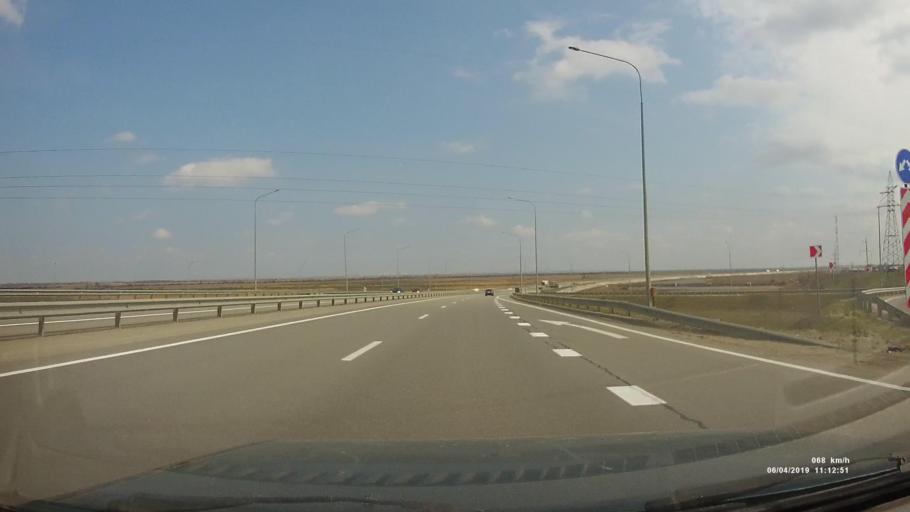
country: RU
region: Rostov
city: Kuleshovka
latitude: 47.0857
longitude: 39.4930
